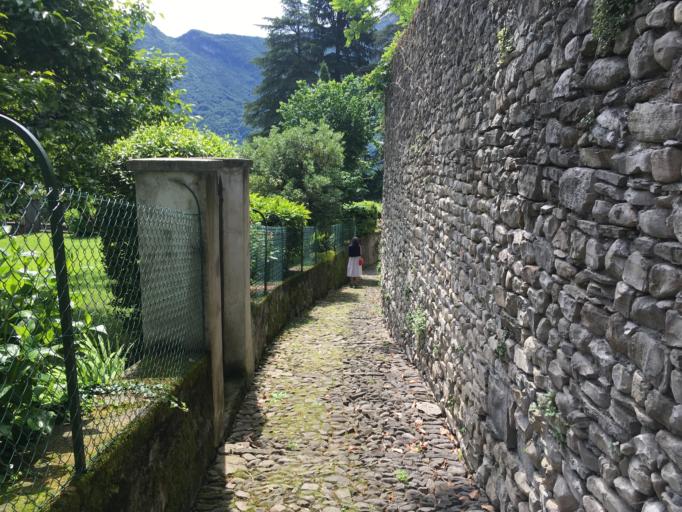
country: IT
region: Lombardy
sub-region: Provincia di Como
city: Lenno
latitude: 45.9684
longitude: 9.1891
